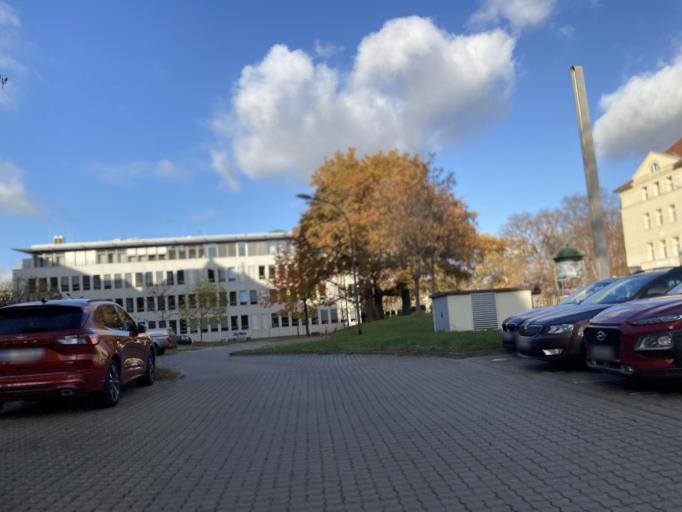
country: DE
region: Saxony-Anhalt
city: Magdeburg
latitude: 52.1334
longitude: 11.6221
